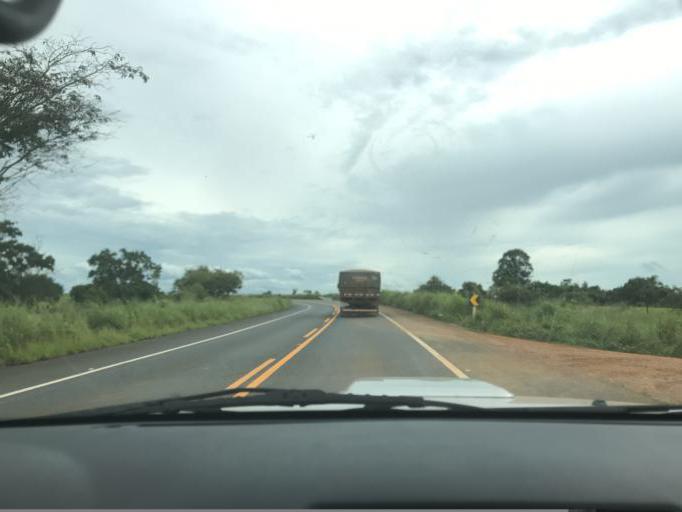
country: BR
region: Minas Gerais
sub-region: Araxa
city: Araxa
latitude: -19.3827
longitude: -46.8600
